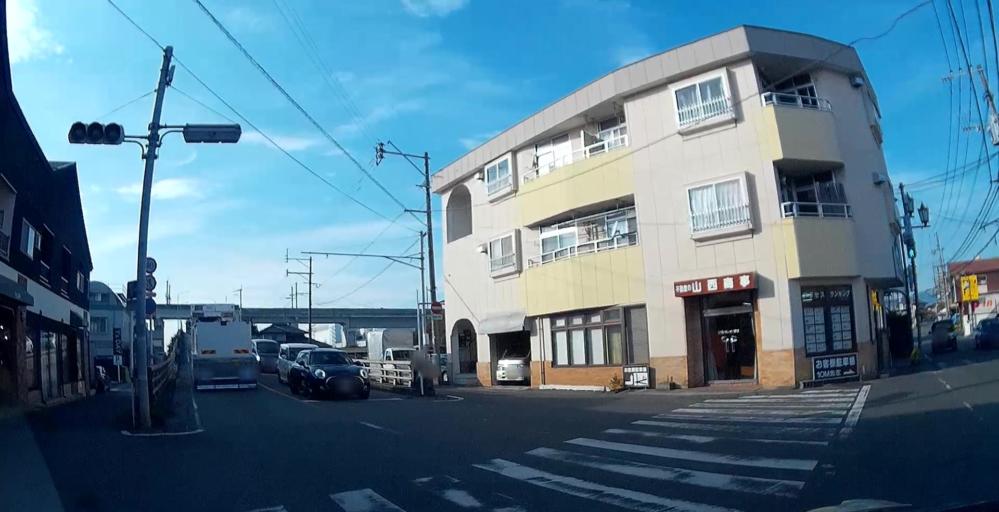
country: JP
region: Kumamoto
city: Kumamoto
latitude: 32.7445
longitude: 130.6813
